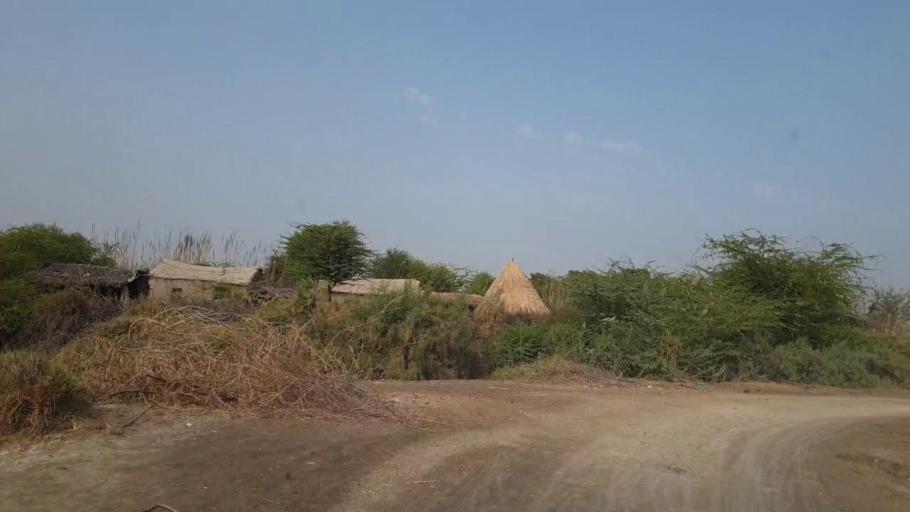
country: PK
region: Sindh
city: Mirpur Khas
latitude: 25.5743
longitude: 69.1544
